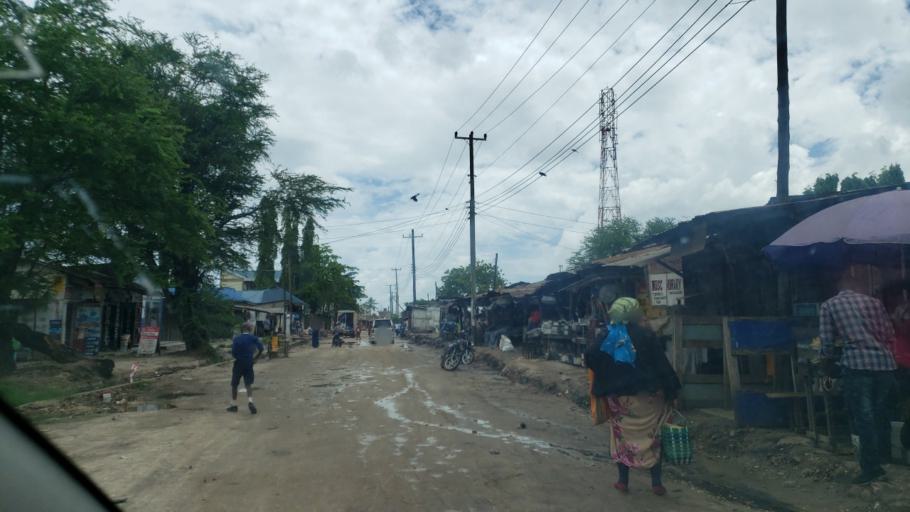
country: TZ
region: Dar es Salaam
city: Magomeni
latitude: -6.8057
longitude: 39.2235
